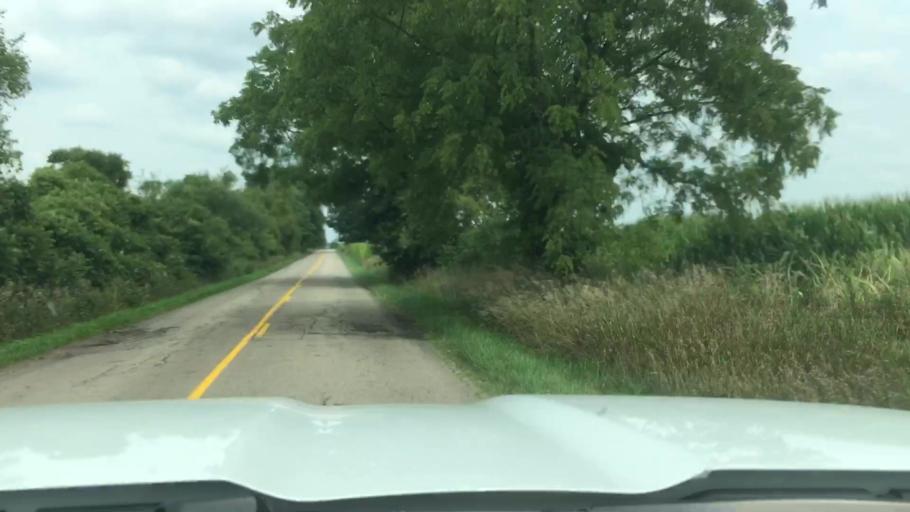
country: US
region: Michigan
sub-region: Ingham County
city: Webberville
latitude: 42.7033
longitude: -84.1912
